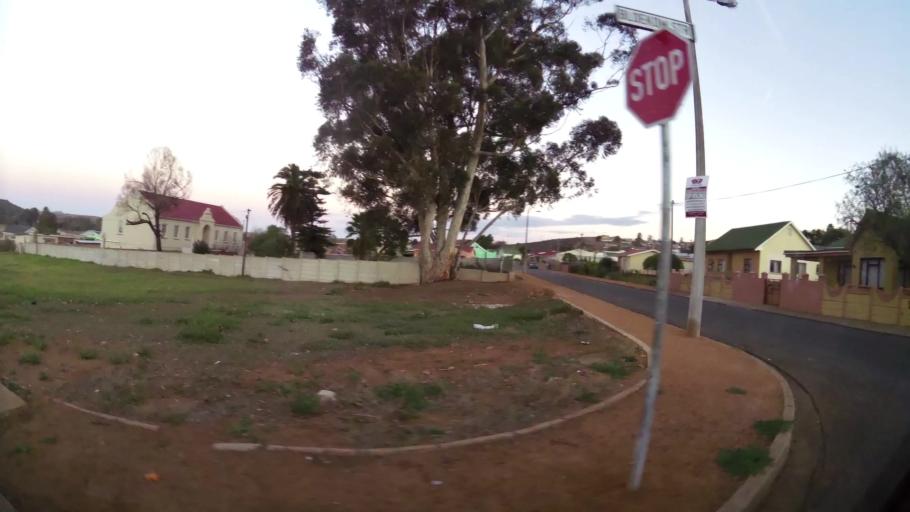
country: ZA
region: Western Cape
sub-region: Eden District Municipality
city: Riversdale
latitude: -34.0964
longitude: 21.2647
